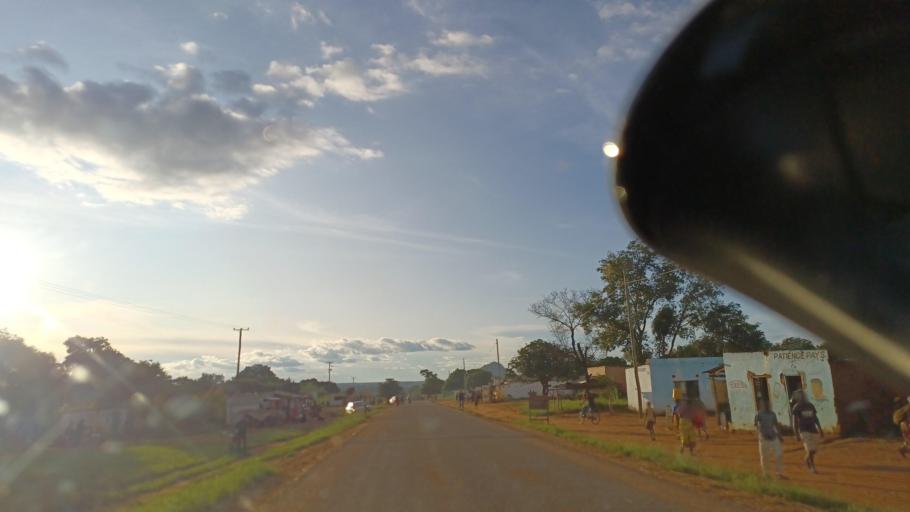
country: ZM
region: North-Western
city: Kasempa
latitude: -13.4616
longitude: 25.8519
